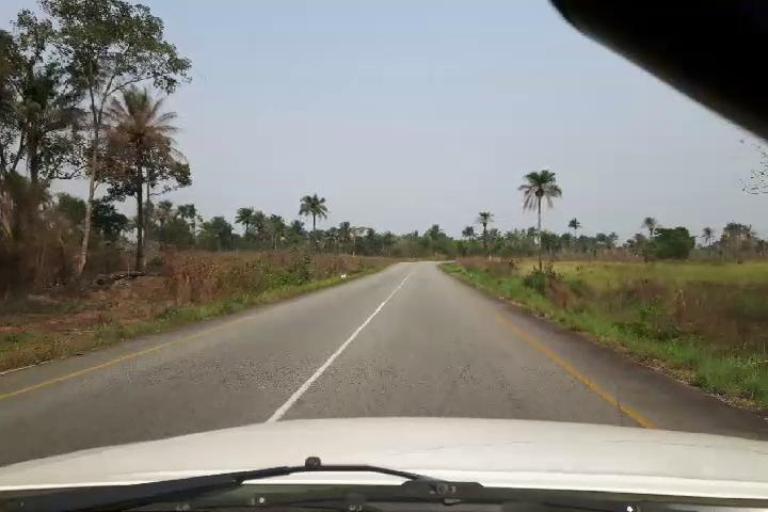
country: SL
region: Southern Province
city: Largo
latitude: 8.3047
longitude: -12.2041
